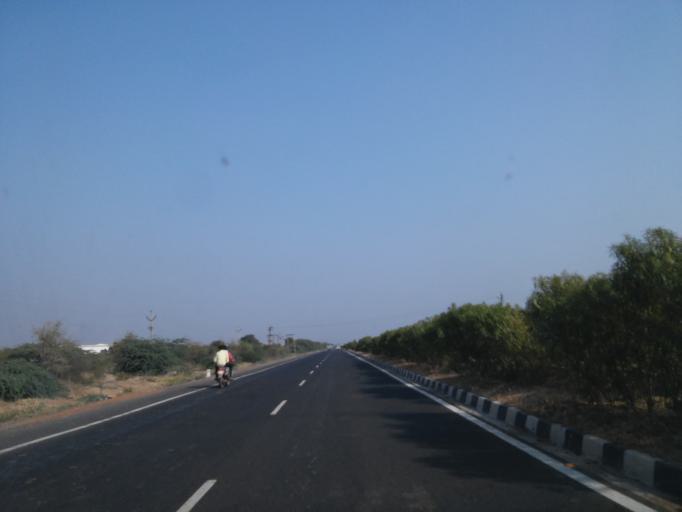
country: IN
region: Gujarat
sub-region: Surendranagar
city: Halvad
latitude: 23.0048
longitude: 71.1477
